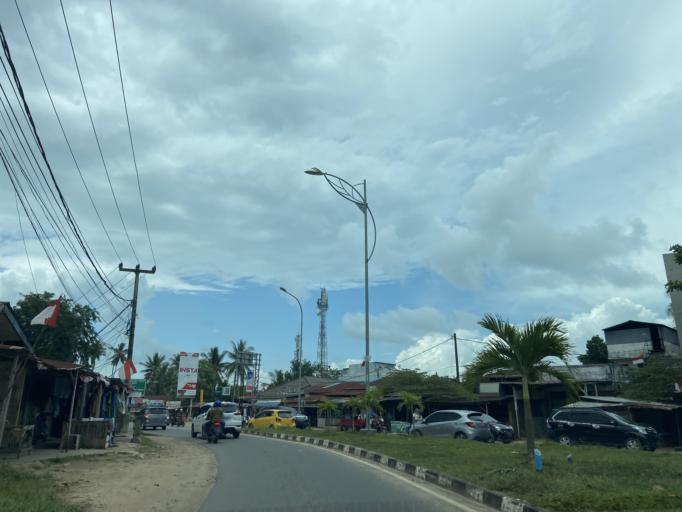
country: SG
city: Singapore
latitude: 1.1493
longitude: 104.1323
